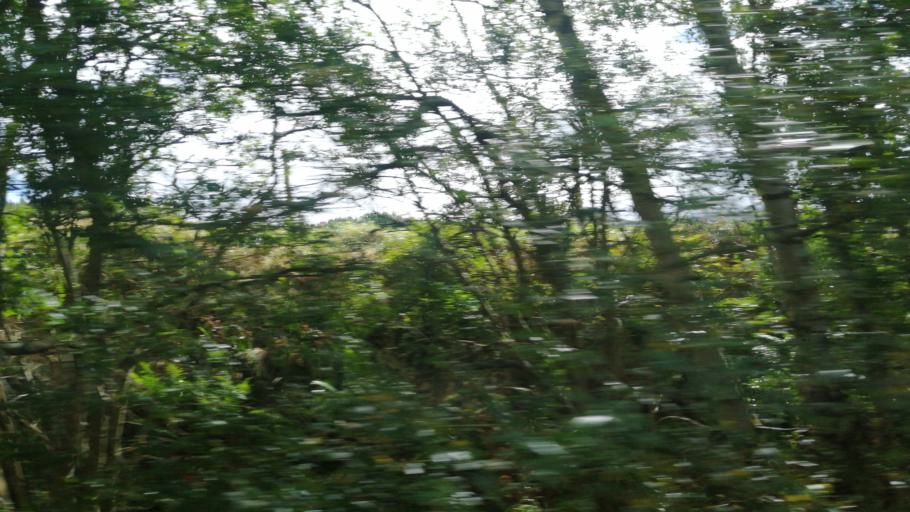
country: GB
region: Scotland
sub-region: Aberdeenshire
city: Insch
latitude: 57.3223
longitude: -2.5418
